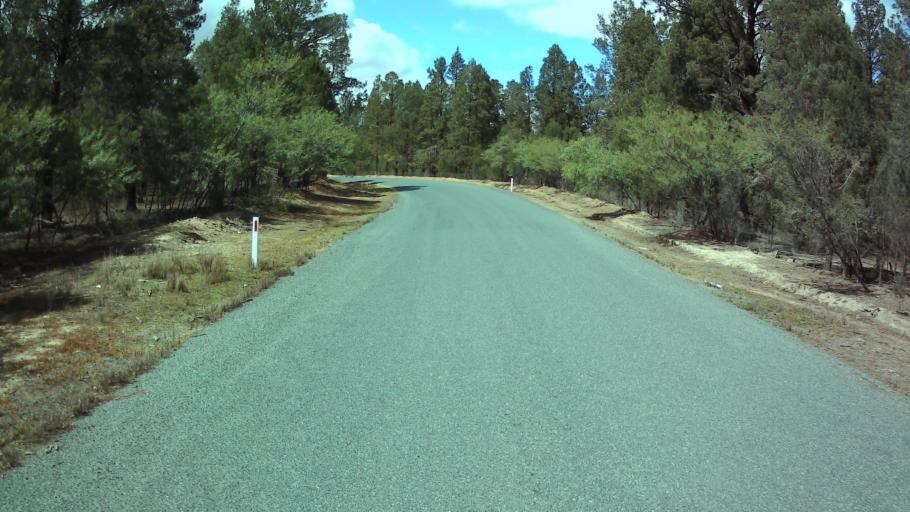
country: AU
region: New South Wales
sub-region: Weddin
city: Grenfell
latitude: -33.9088
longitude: 147.9193
